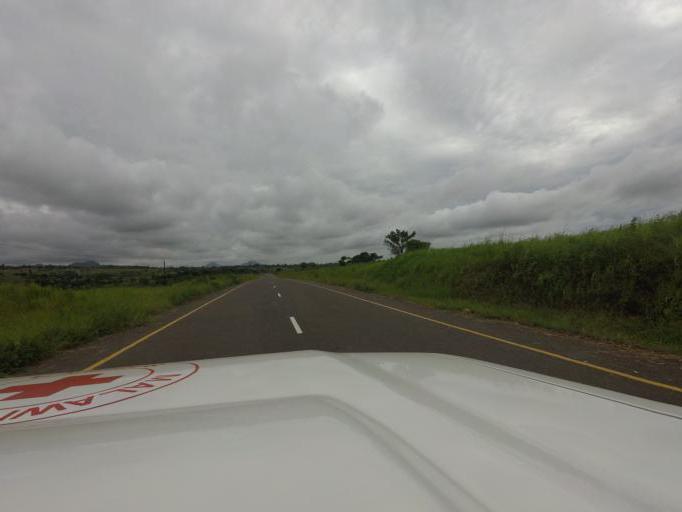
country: MW
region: Southern Region
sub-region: Thyolo District
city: Thyolo
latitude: -16.0034
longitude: 35.1780
